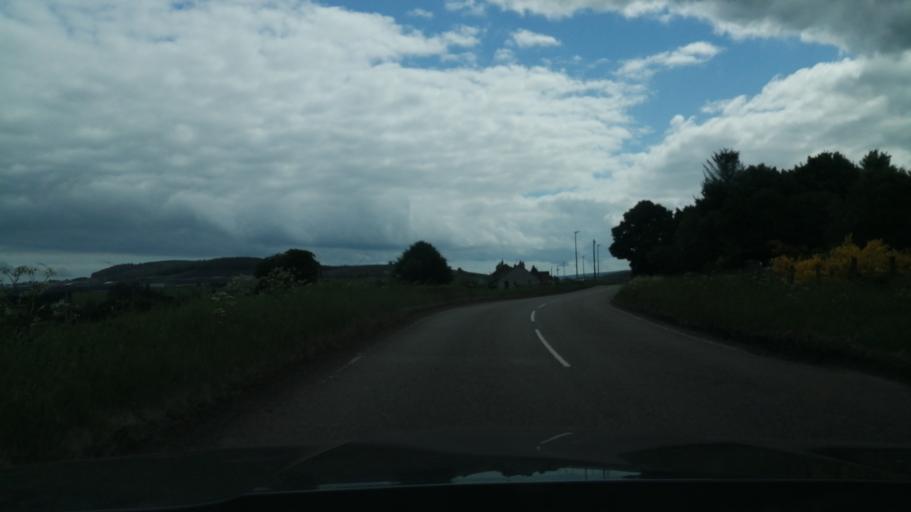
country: GB
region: Scotland
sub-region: Moray
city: Fochabers
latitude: 57.5464
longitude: -3.0953
